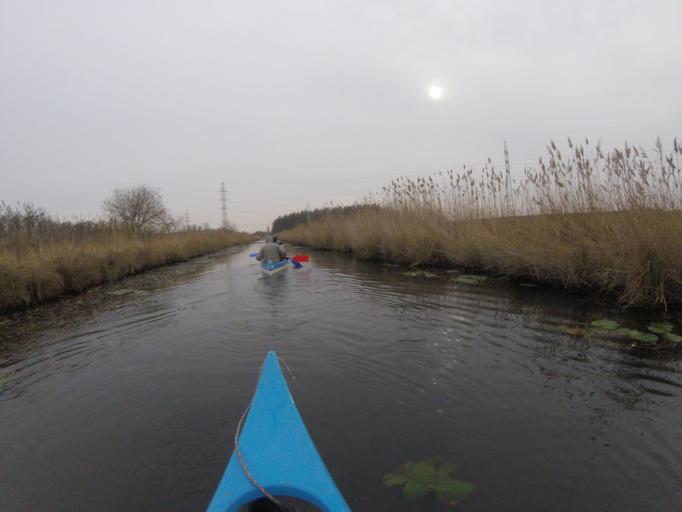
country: HU
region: Zala
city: Heviz
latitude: 46.7706
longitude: 17.2050
